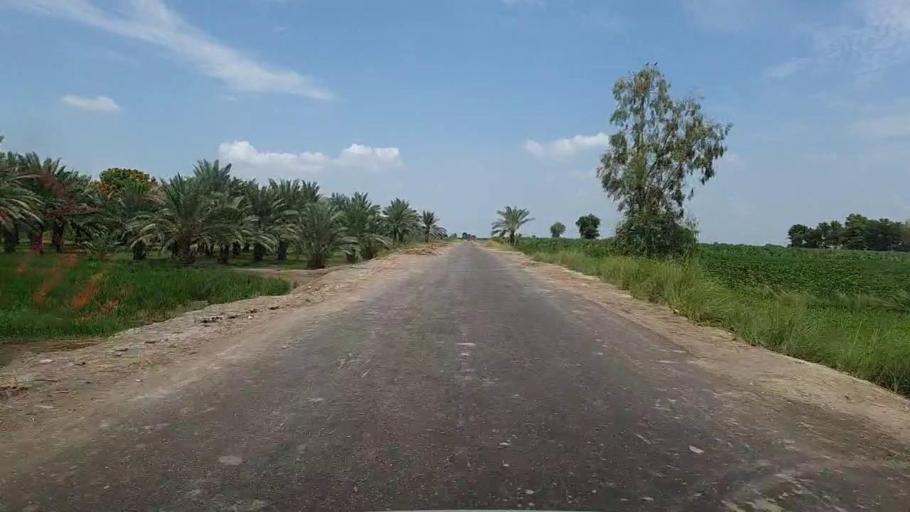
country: PK
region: Sindh
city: Bhiria
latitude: 26.9330
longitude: 68.2151
